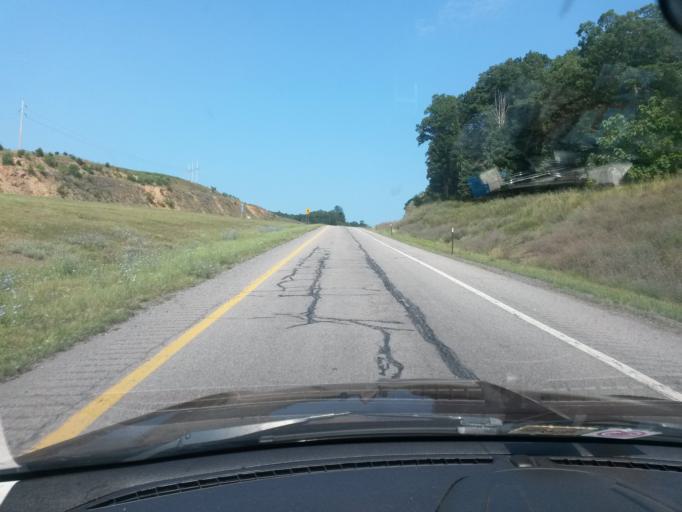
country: US
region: West Virginia
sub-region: Hardy County
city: Moorefield
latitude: 39.0467
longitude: -78.7406
